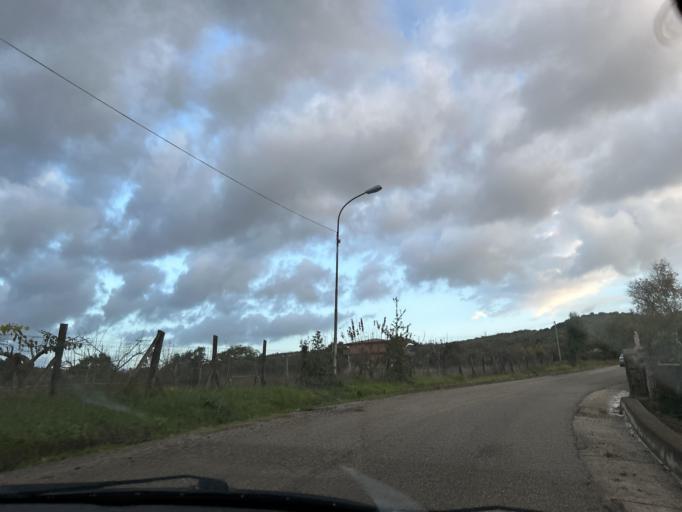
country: IT
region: Calabria
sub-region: Provincia di Catanzaro
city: Squillace
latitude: 38.7731
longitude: 16.5063
